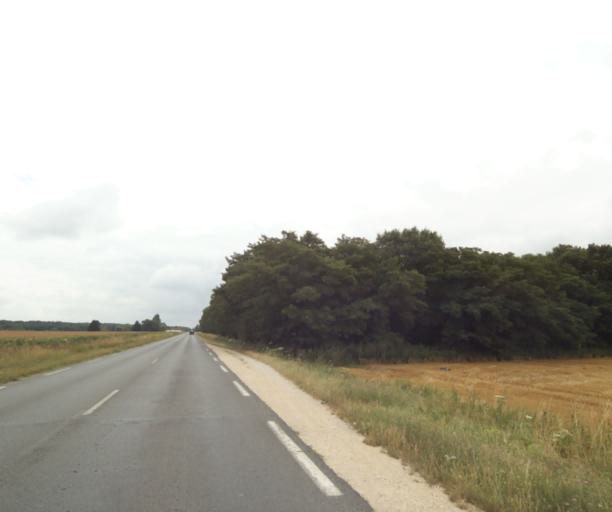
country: FR
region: Centre
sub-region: Departement du Loiret
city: Mardie
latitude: 47.8854
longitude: 2.0747
